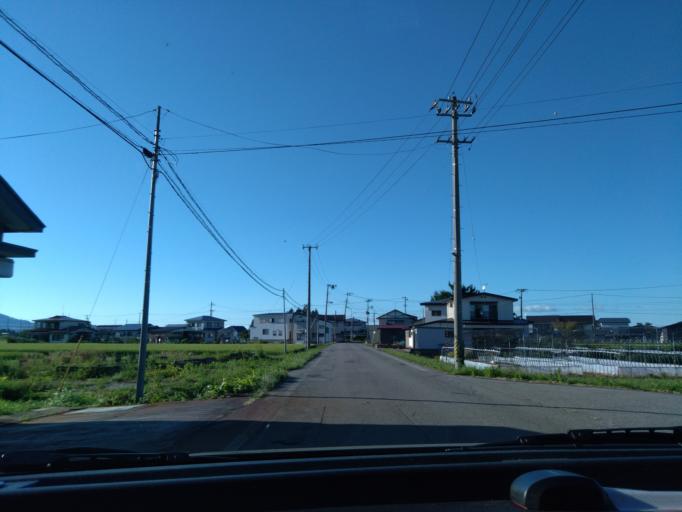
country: JP
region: Akita
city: Omagari
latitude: 39.4206
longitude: 140.5144
